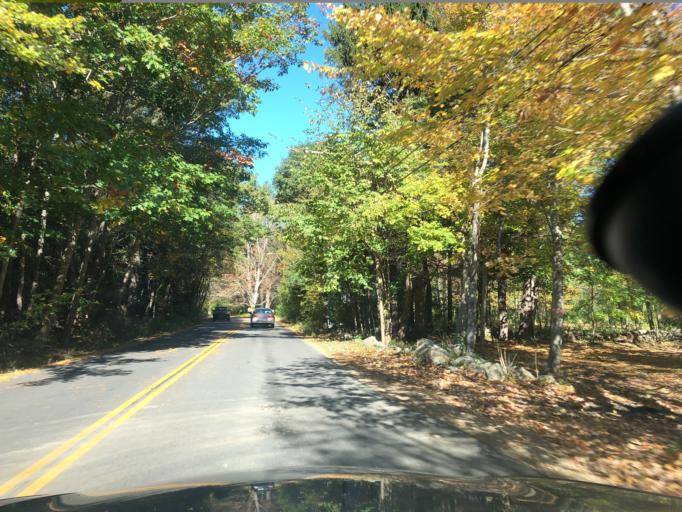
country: US
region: New Hampshire
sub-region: Rockingham County
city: Newmarket
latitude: 43.1109
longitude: -70.9600
